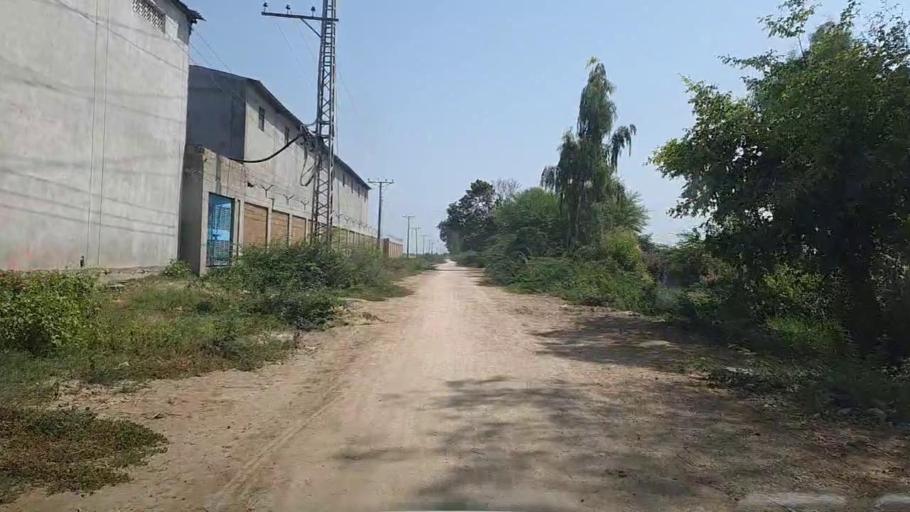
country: PK
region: Sindh
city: Kario
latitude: 24.6346
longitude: 68.5367
